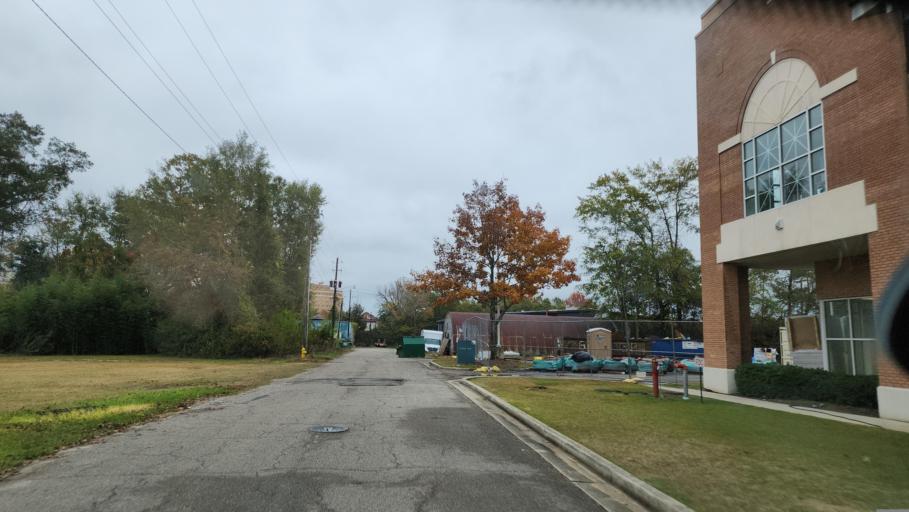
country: US
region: Mississippi
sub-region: Forrest County
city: Hattiesburg
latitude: 31.3257
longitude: -89.2958
